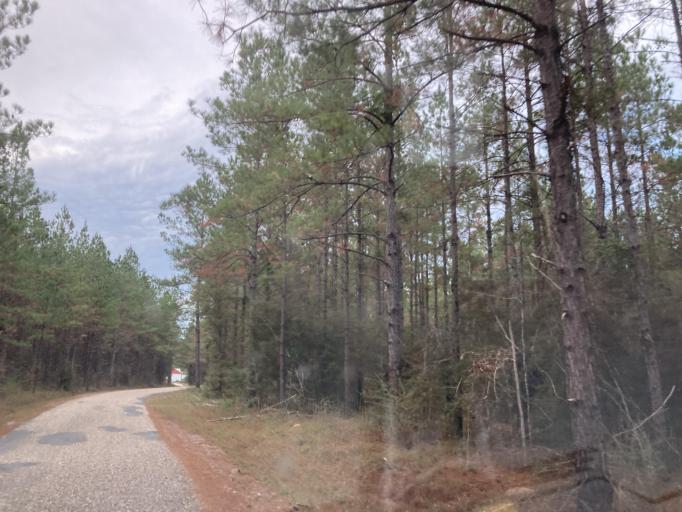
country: US
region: Mississippi
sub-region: Lamar County
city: Purvis
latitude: 31.1748
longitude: -89.3910
